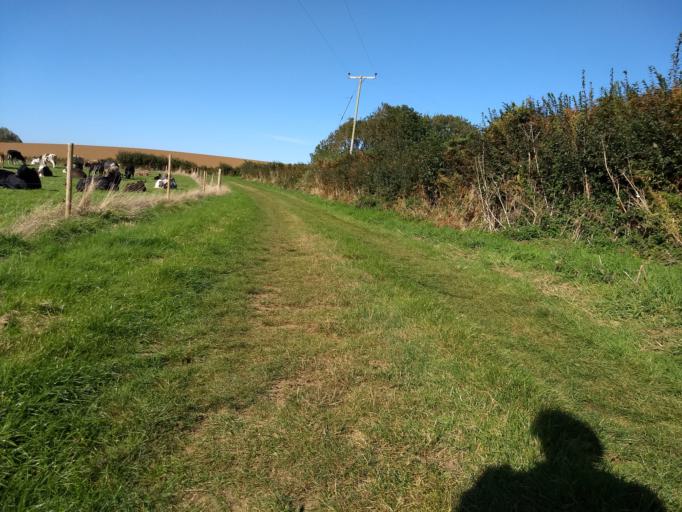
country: GB
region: England
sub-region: Isle of Wight
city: Niton
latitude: 50.6390
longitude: -1.2840
